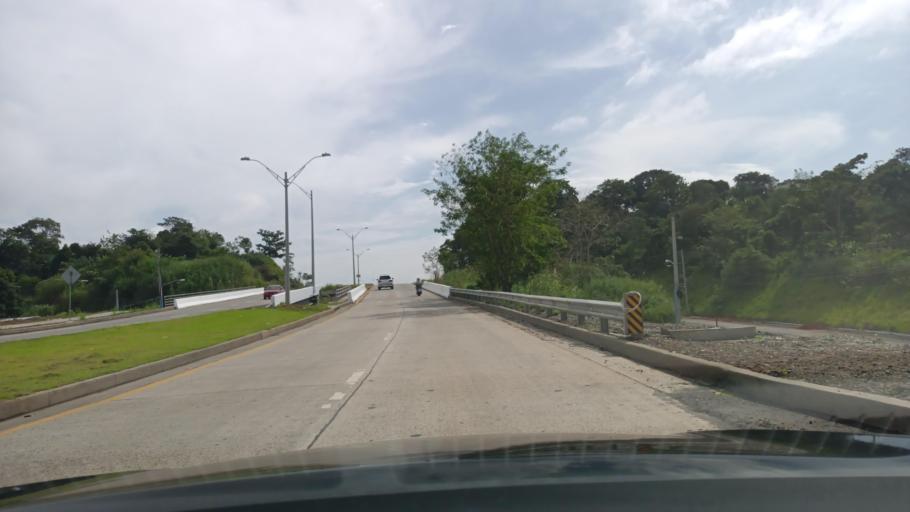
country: PA
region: Panama
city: Las Cumbres
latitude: 9.0990
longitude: -79.5133
